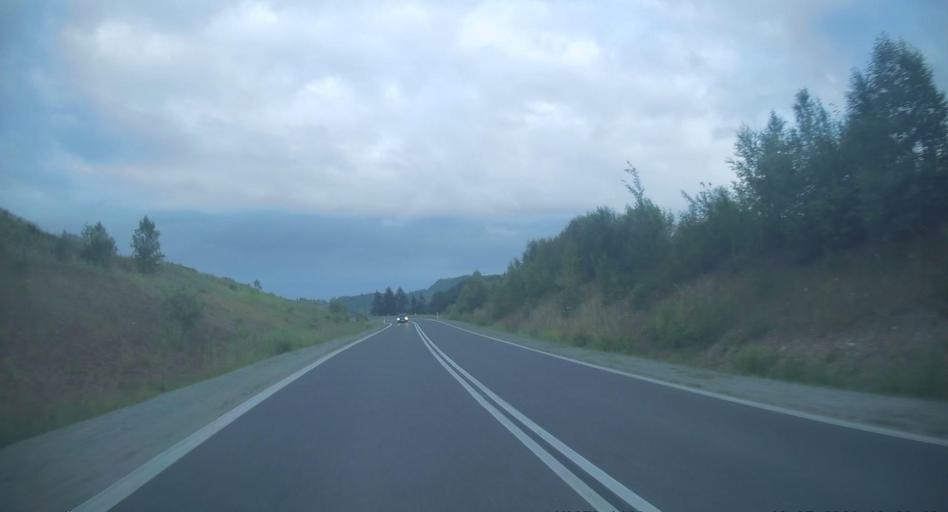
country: PL
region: Lower Silesian Voivodeship
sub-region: Powiat klodzki
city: Nowa Ruda
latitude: 50.6000
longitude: 16.5118
